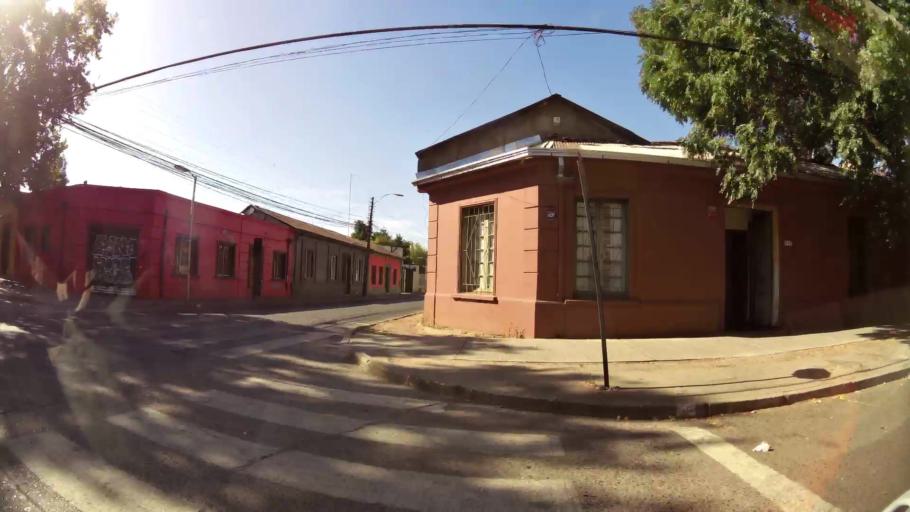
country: CL
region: Maule
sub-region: Provincia de Talca
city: Talca
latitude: -35.4268
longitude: -71.6694
